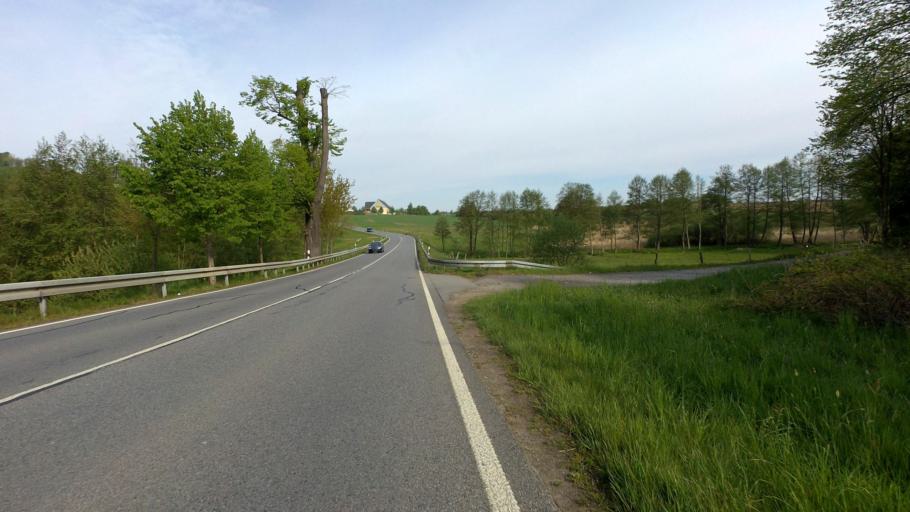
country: DE
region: Saxony
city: Stolpen
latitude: 51.0477
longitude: 14.0946
